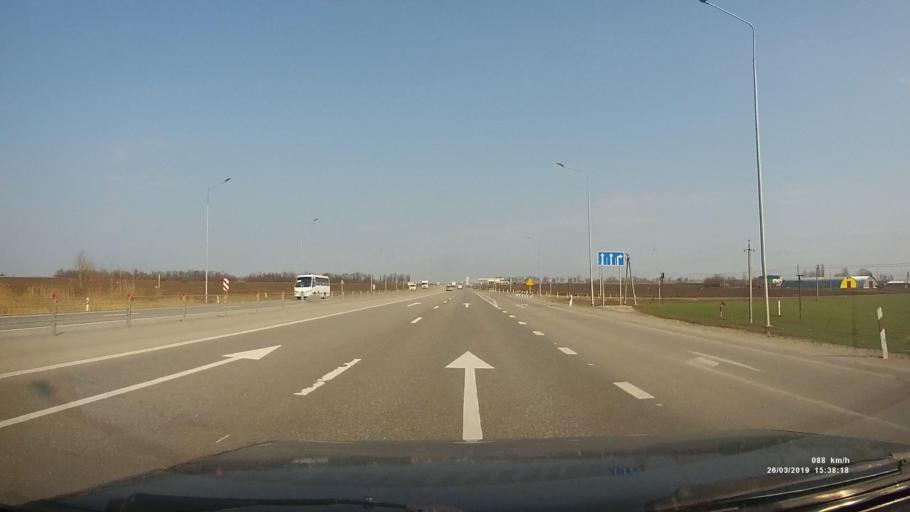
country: RU
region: Rostov
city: Sinyavskoye
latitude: 47.2944
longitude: 39.2675
